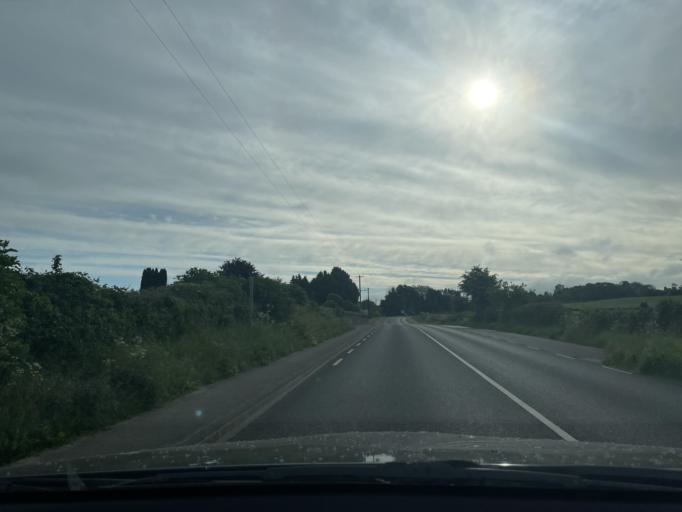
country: IE
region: Leinster
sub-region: County Carlow
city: Bagenalstown
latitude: 52.6324
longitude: -6.9819
